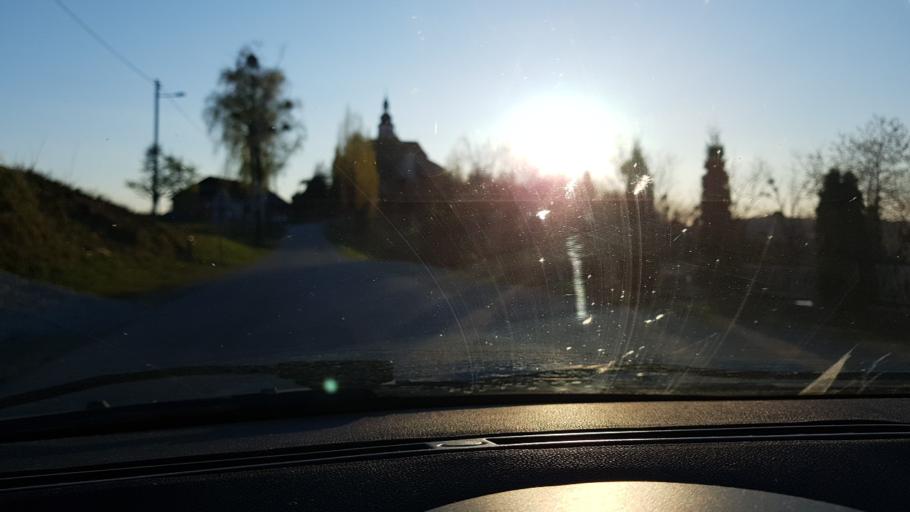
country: HR
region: Krapinsko-Zagorska
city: Pregrada
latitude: 46.1668
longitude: 15.7006
